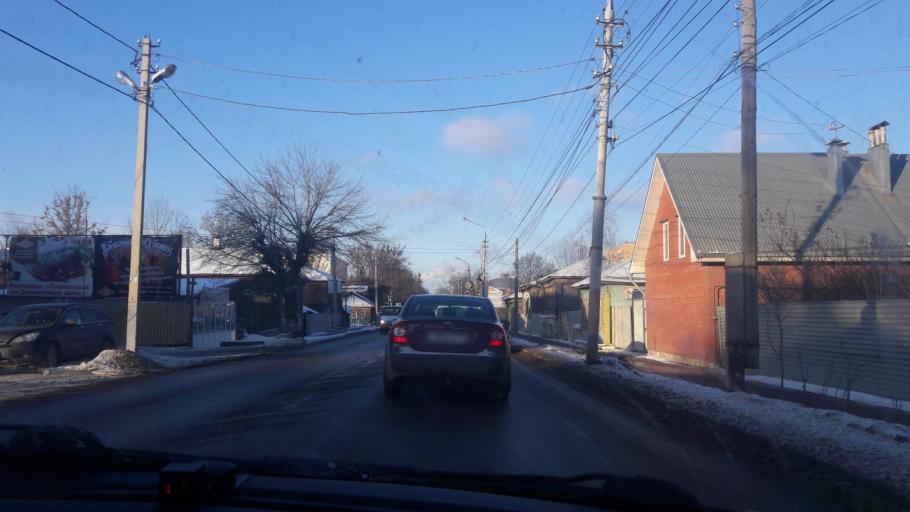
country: RU
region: Tula
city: Tula
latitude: 54.1848
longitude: 37.6274
